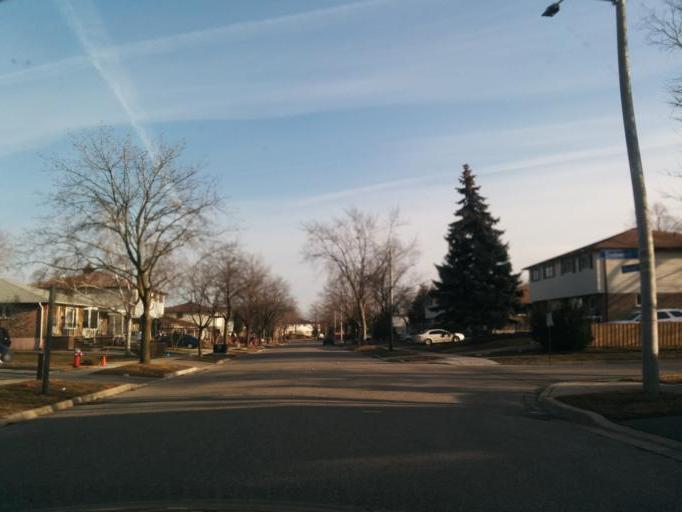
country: CA
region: Ontario
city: Mississauga
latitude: 43.5999
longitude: -79.6023
